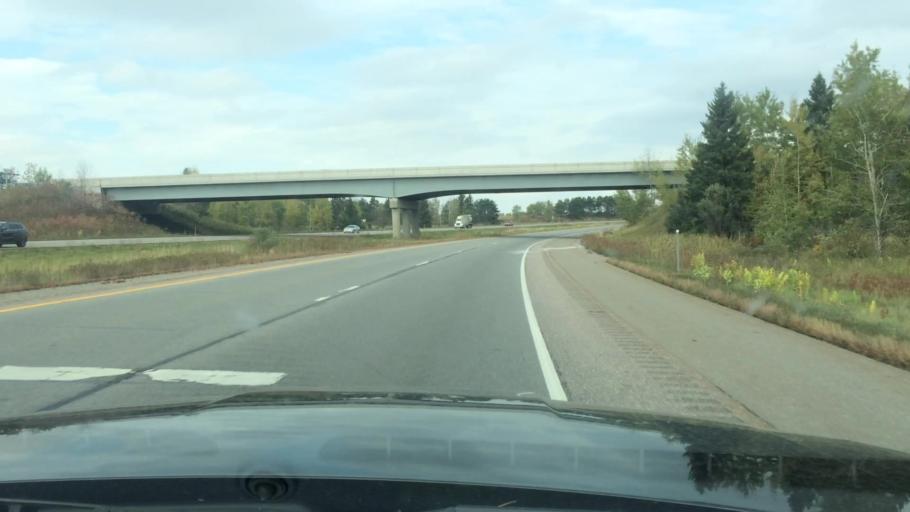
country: US
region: Wisconsin
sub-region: Marathon County
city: Mosinee
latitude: 44.7282
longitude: -89.6777
